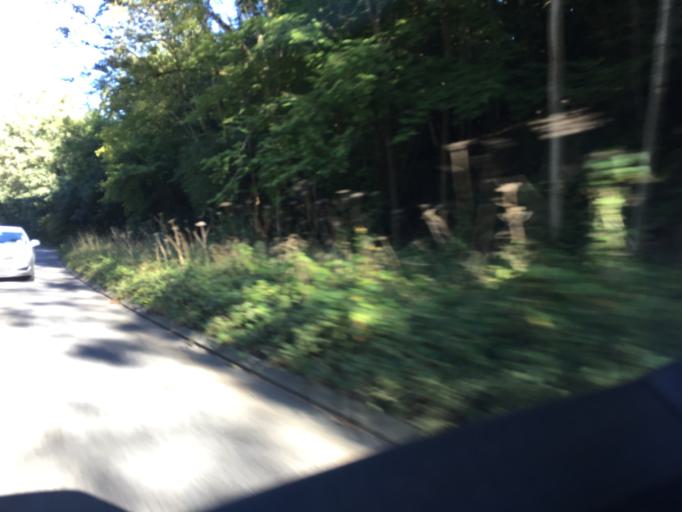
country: GB
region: England
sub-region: Wiltshire
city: Biddestone
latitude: 51.4719
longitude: -2.2188
